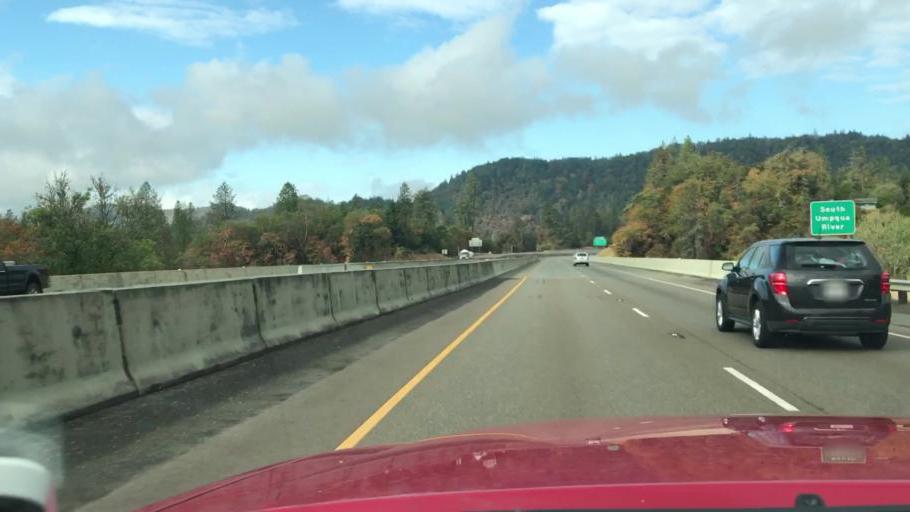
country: US
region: Oregon
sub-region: Douglas County
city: Tri-City
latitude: 42.9480
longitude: -123.3222
